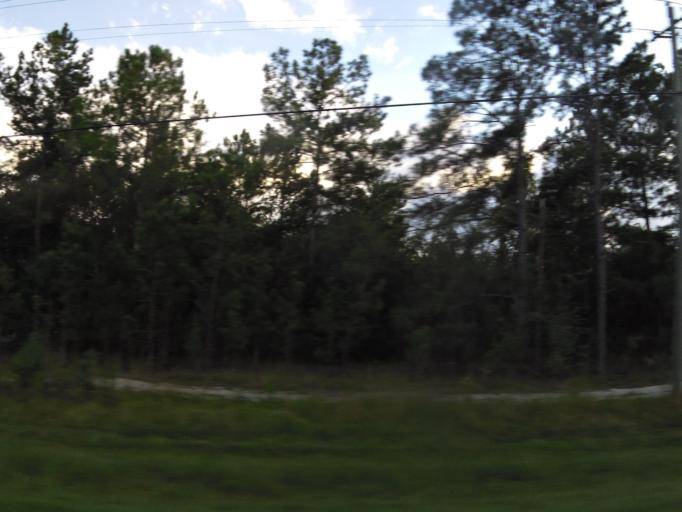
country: US
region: Georgia
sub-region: Echols County
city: Statenville
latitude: 30.7730
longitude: -83.1442
